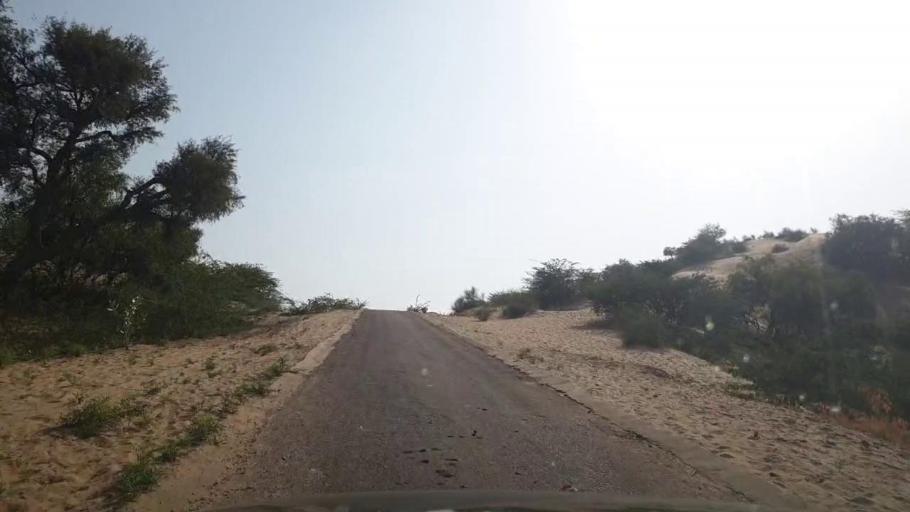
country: PK
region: Sindh
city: Islamkot
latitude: 25.1181
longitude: 70.5114
